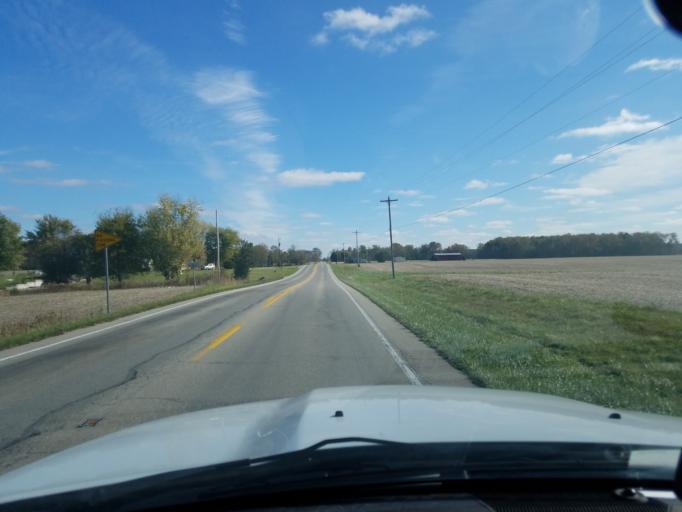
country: US
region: Indiana
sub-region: Ripley County
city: Osgood
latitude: 39.0749
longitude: -85.3678
